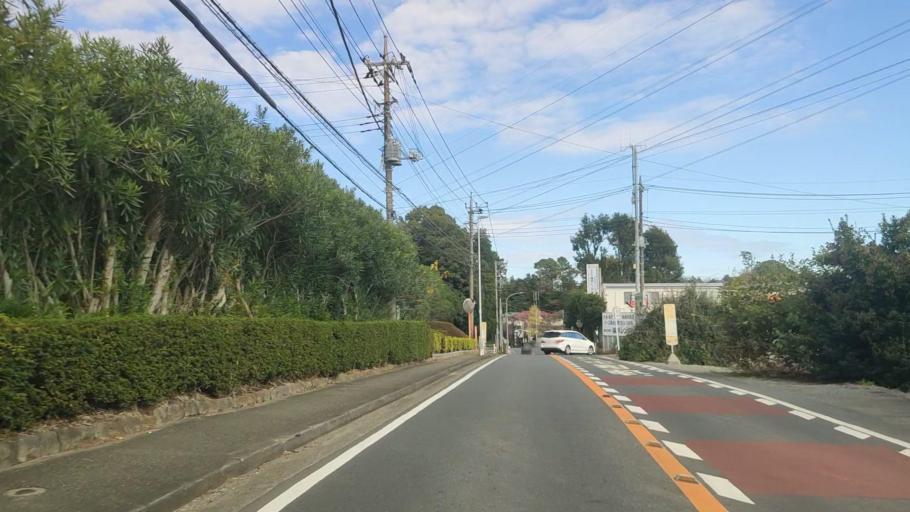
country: JP
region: Kanagawa
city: Minami-rinkan
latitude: 35.4888
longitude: 139.5042
